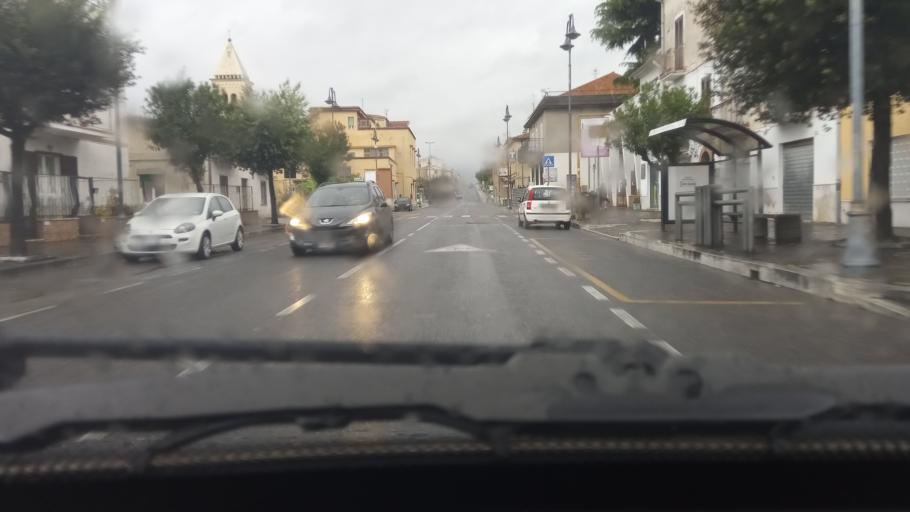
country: IT
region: Latium
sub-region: Provincia di Latina
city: Penitro
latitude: 41.2583
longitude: 13.7005
